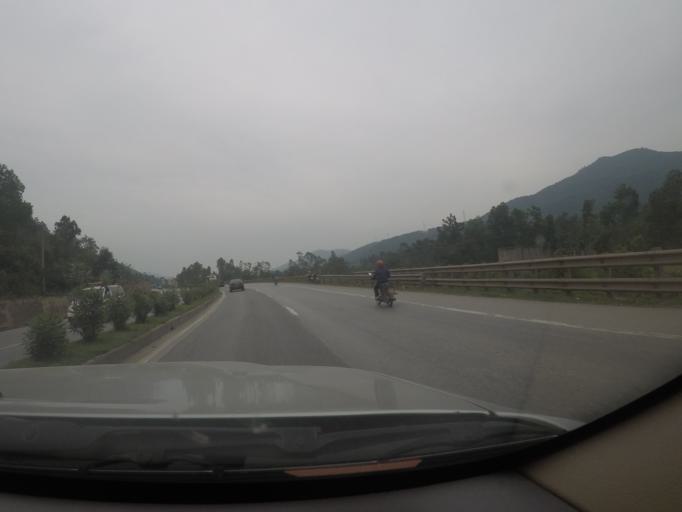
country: VN
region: Nghe An
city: Dien Chau
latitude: 18.8808
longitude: 105.6048
